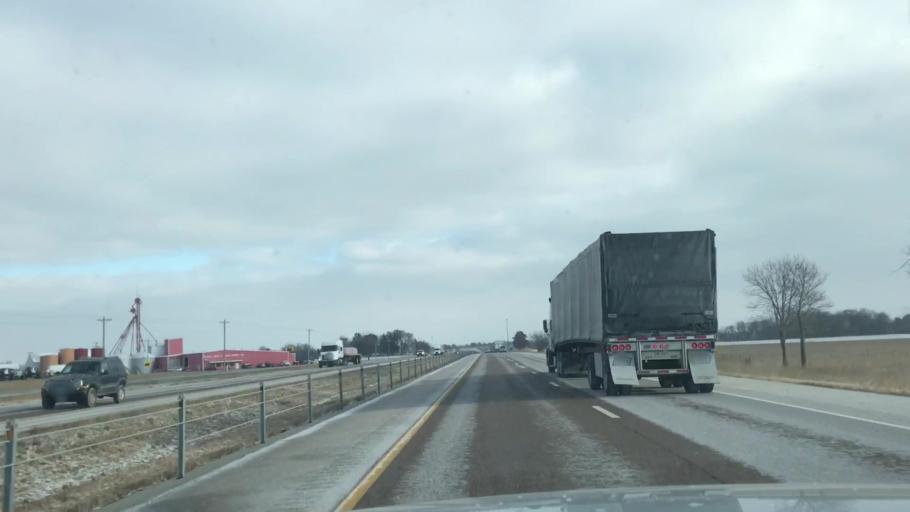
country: US
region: Illinois
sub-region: Madison County
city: Worden
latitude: 38.9222
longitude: -89.8106
